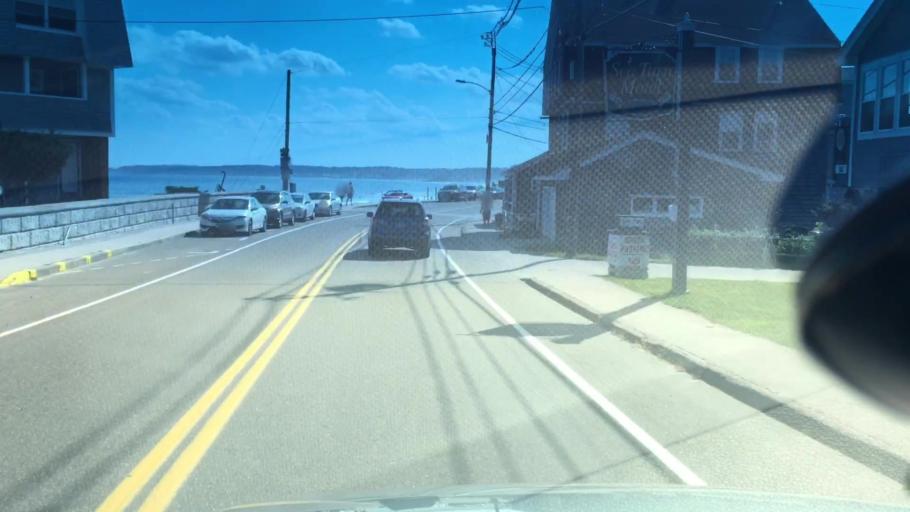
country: US
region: Maine
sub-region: York County
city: York Beach
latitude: 43.1695
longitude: -70.6117
